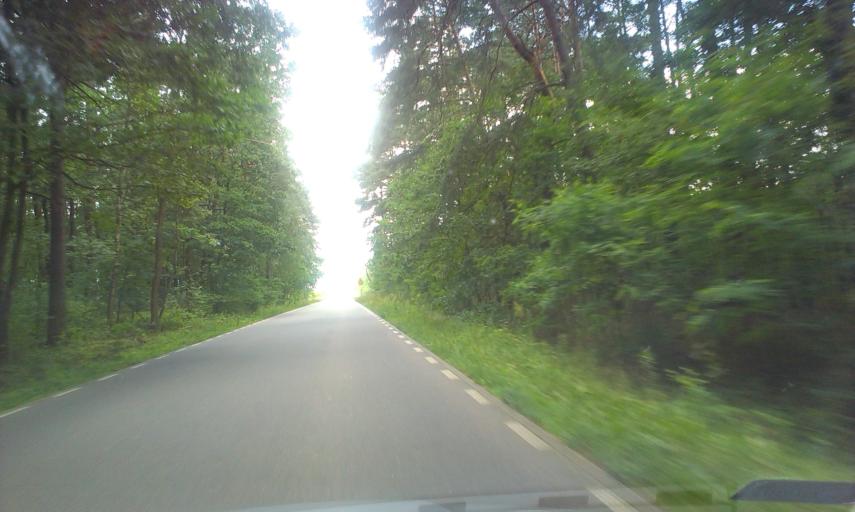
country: PL
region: Masovian Voivodeship
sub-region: Powiat zyrardowski
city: Radziejowice
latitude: 51.9689
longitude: 20.5844
